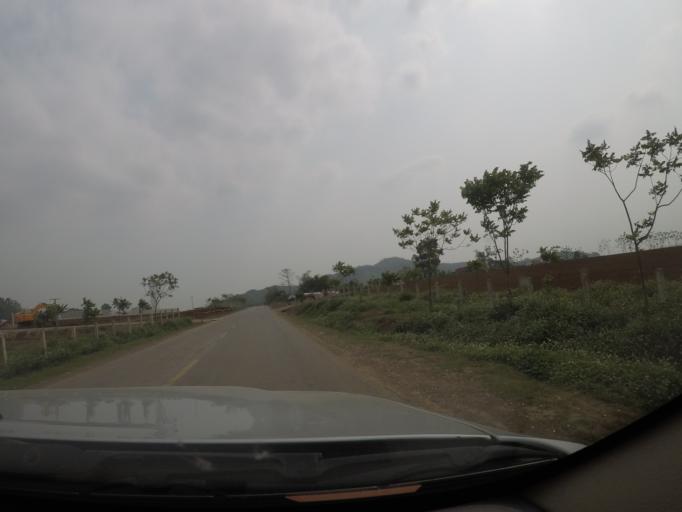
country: VN
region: Thanh Hoa
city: Thi Tran Ben Sung
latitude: 19.3991
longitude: 105.4542
